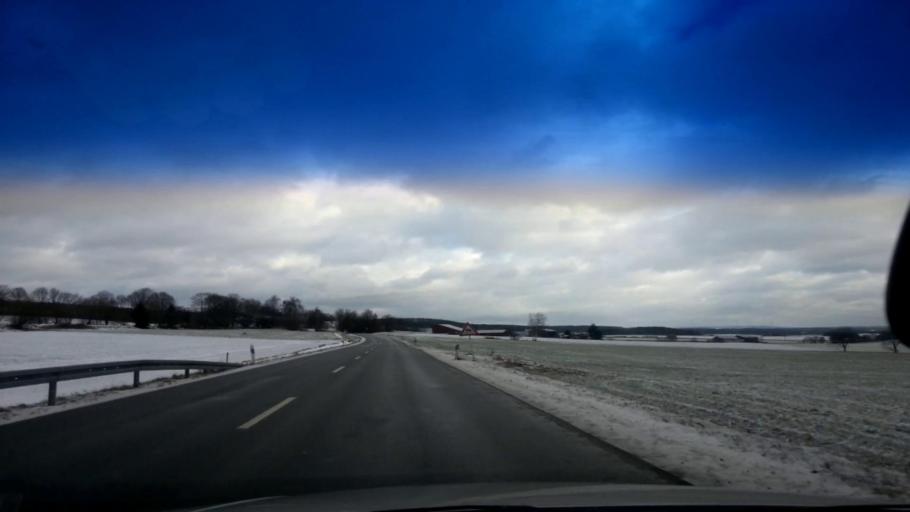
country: DE
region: Bavaria
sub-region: Upper Franconia
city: Grub
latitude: 50.1244
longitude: 11.9133
